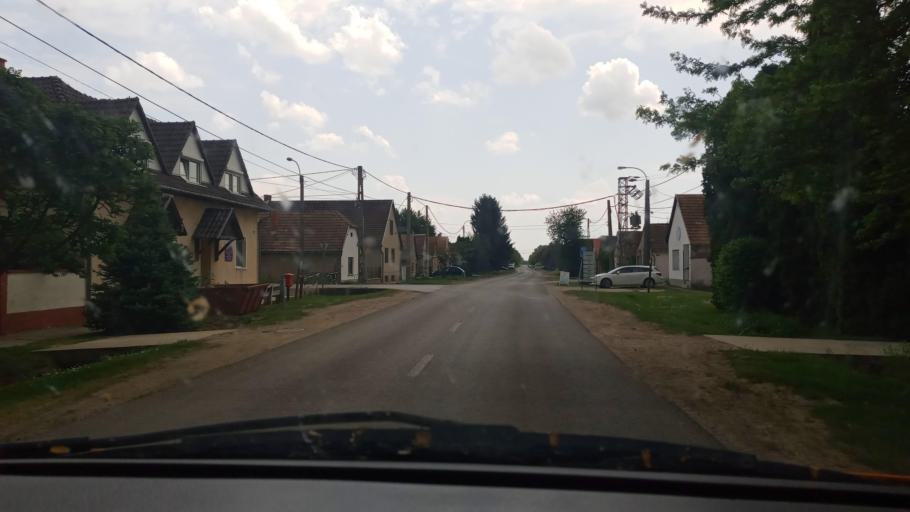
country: HU
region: Baranya
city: Beremend
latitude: 45.7804
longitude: 18.4381
